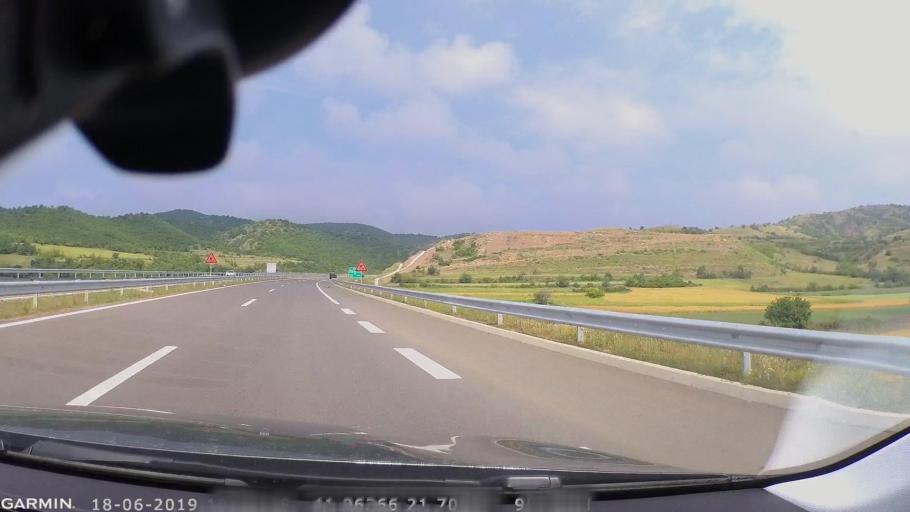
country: MK
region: Petrovec
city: Sredno Konjare
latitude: 41.9472
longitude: 21.8013
